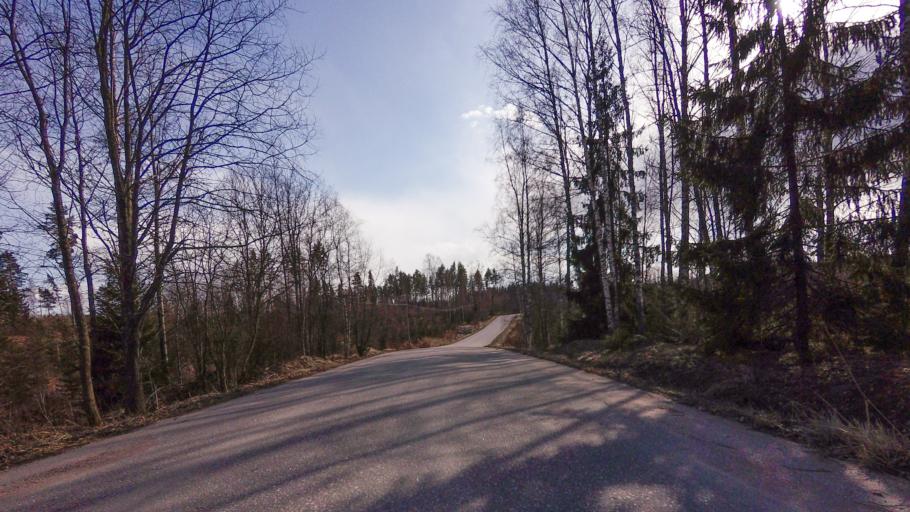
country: FI
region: Varsinais-Suomi
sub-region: Salo
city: Suomusjaervi
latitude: 60.2980
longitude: 23.6415
